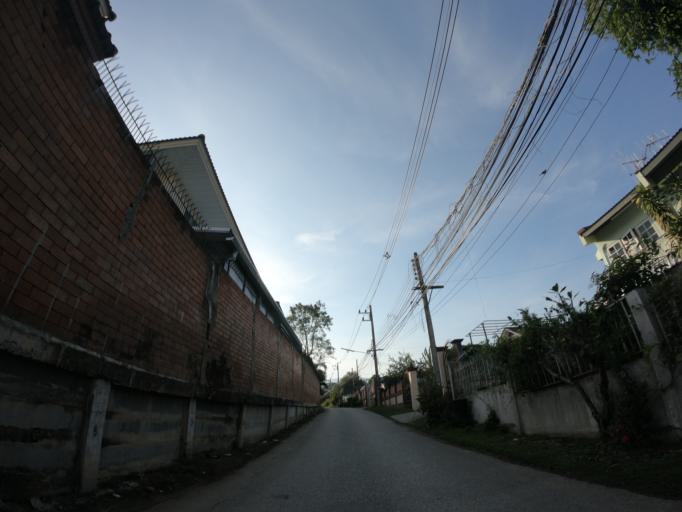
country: TH
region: Chiang Mai
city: Chiang Mai
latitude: 18.8337
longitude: 98.9791
